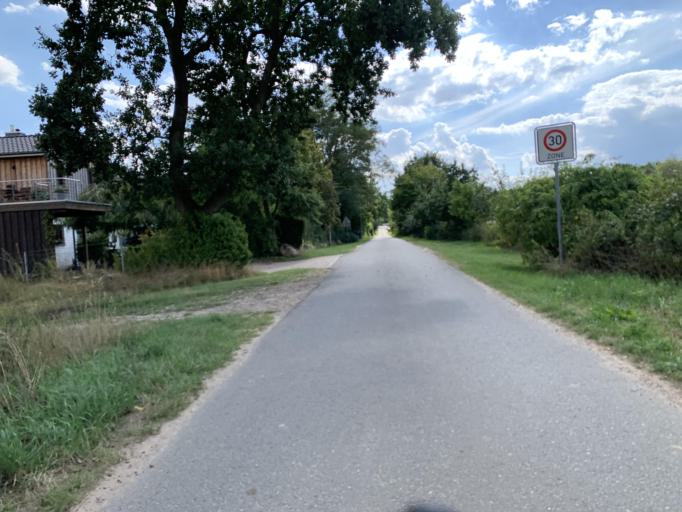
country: DE
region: Lower Saxony
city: Reinstorf
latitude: 53.2175
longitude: 10.5921
